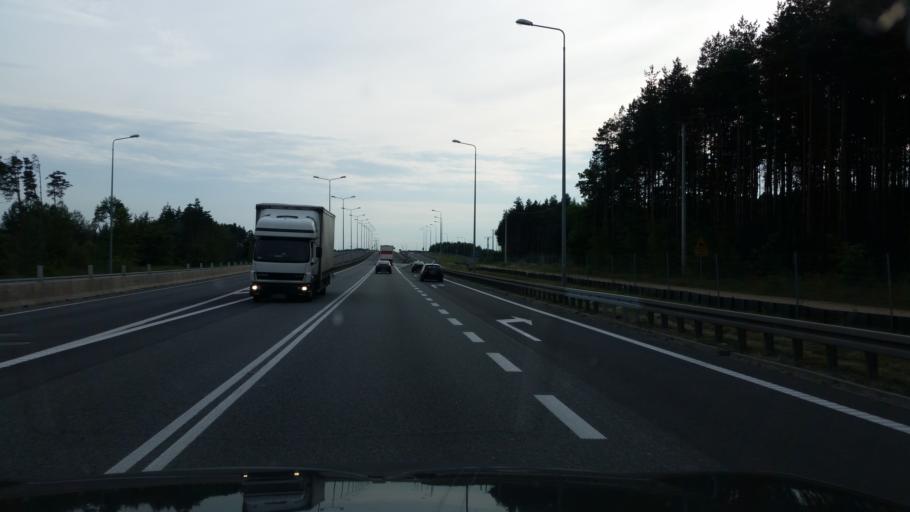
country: PL
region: Silesian Voivodeship
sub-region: Powiat bedzinski
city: Mierzecice
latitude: 50.4560
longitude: 19.0886
